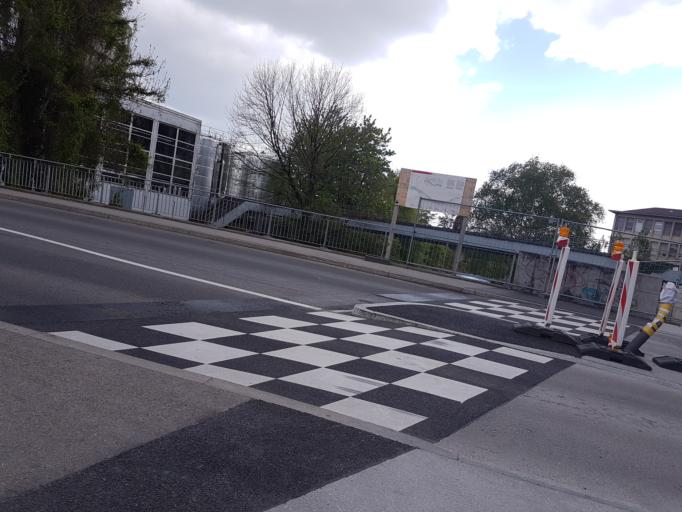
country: CH
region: Bern
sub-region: Biel/Bienne District
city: Biel/Bienne
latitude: 47.1438
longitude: 7.2617
